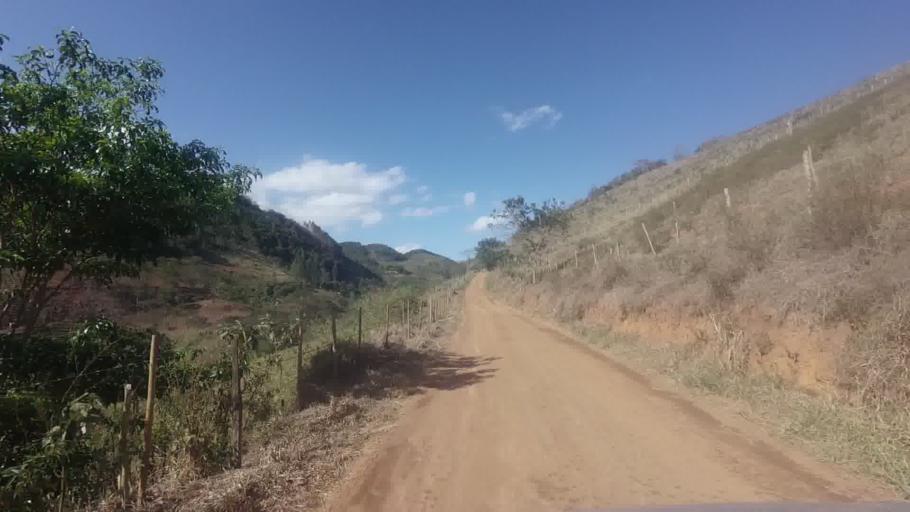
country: BR
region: Espirito Santo
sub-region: Sao Jose Do Calcado
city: Sao Jose do Calcado
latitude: -21.0307
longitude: -41.5853
